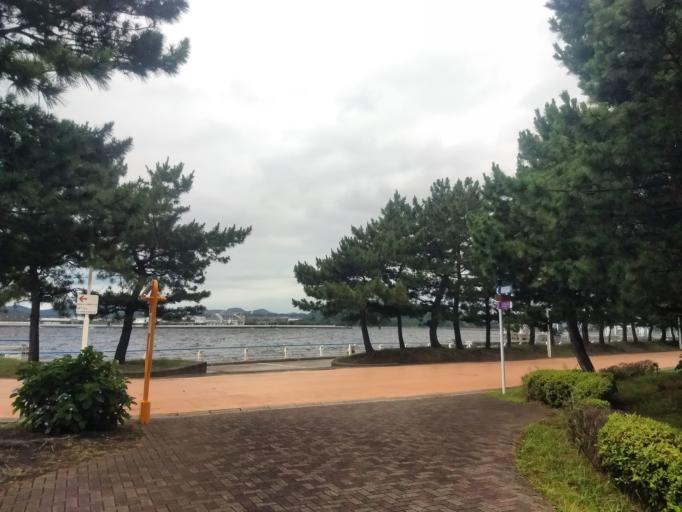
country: JP
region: Kanagawa
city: Yokosuka
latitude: 35.3346
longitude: 139.6459
